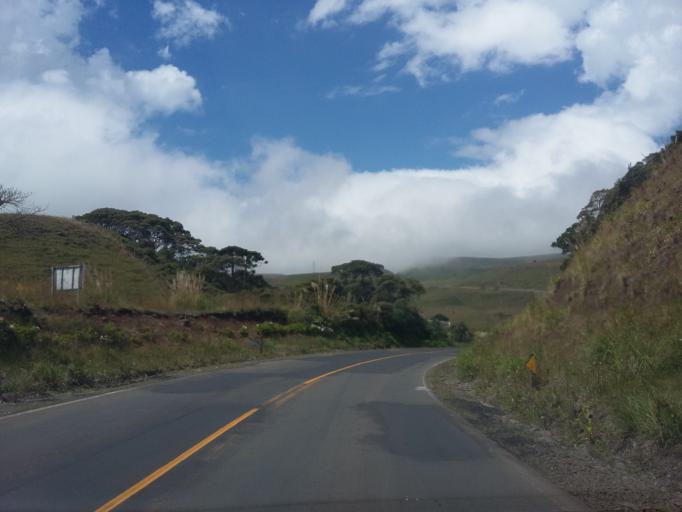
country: BR
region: Santa Catarina
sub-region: Lauro Muller
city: Lauro Muller
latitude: -28.3689
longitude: -49.5726
